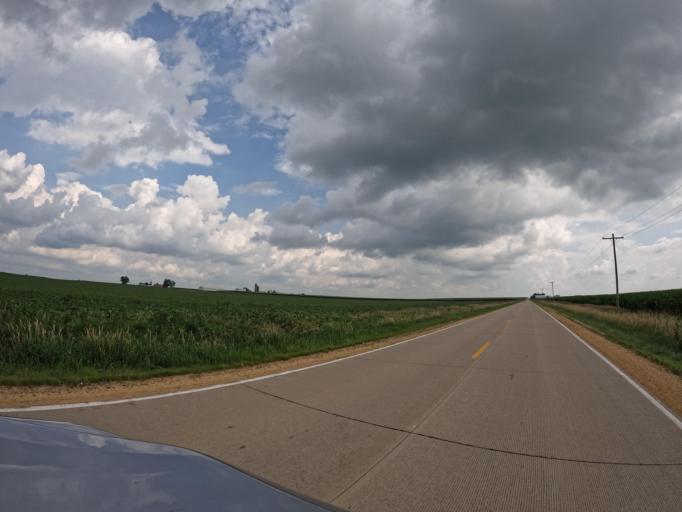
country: US
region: Iowa
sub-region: Clinton County
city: De Witt
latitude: 41.7824
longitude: -90.4131
